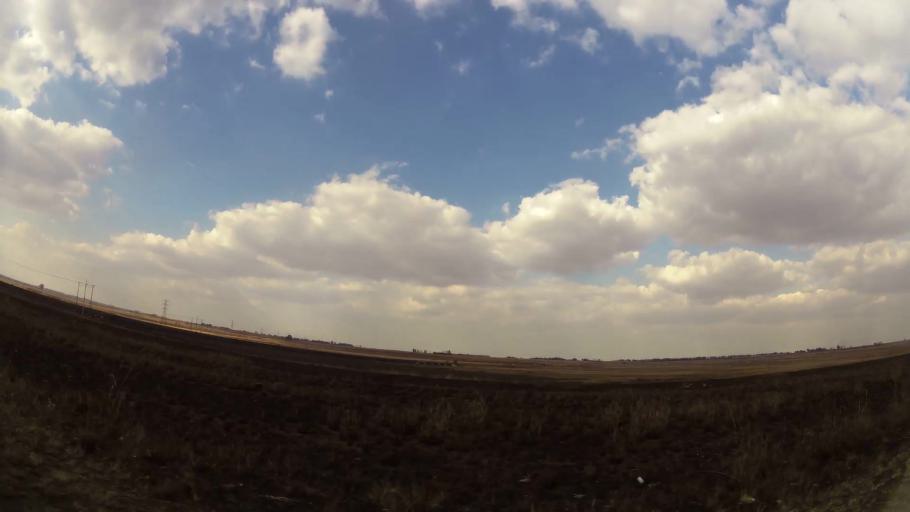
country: ZA
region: Mpumalanga
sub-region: Nkangala District Municipality
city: Delmas
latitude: -26.1780
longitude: 28.6965
